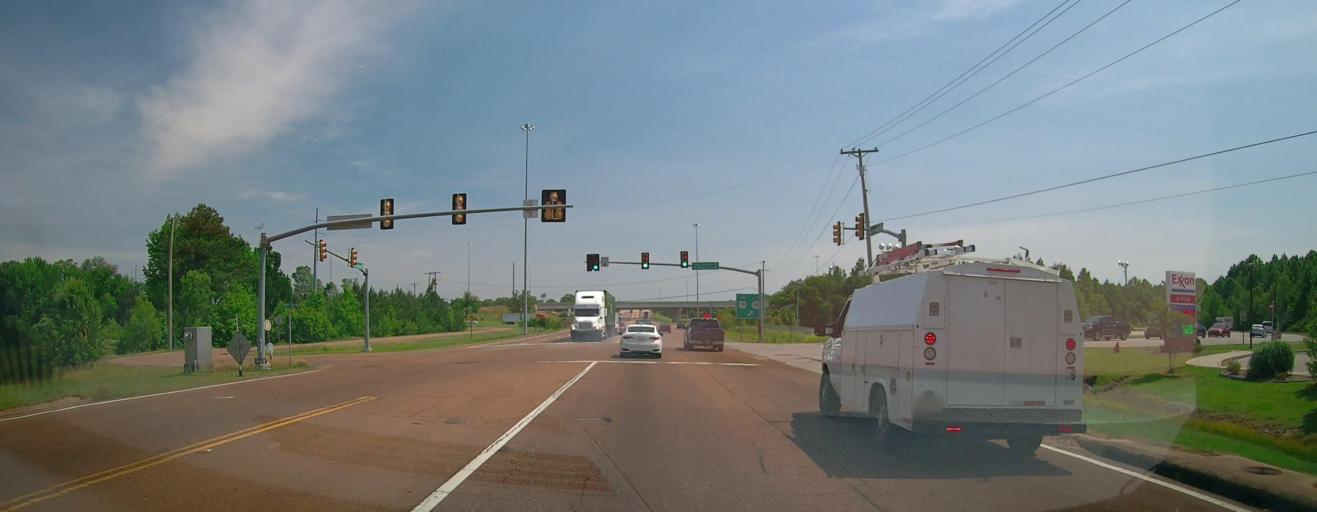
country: US
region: Mississippi
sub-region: De Soto County
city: Olive Branch
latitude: 34.9731
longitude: -89.8306
